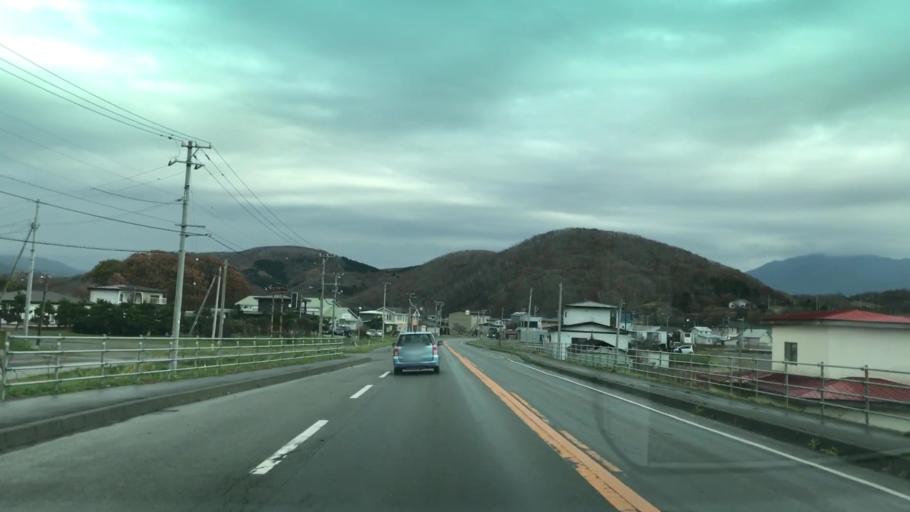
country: JP
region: Hokkaido
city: Shizunai-furukawacho
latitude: 42.1333
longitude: 142.9039
